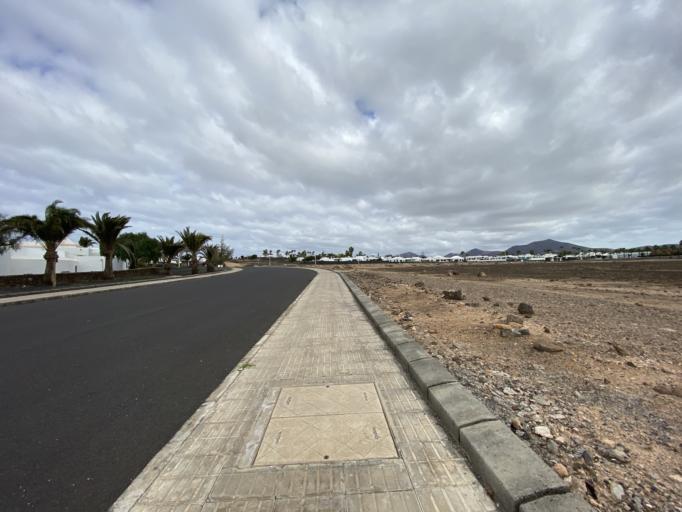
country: ES
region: Canary Islands
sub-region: Provincia de Las Palmas
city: Playa Blanca
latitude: 28.8628
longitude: -13.8463
